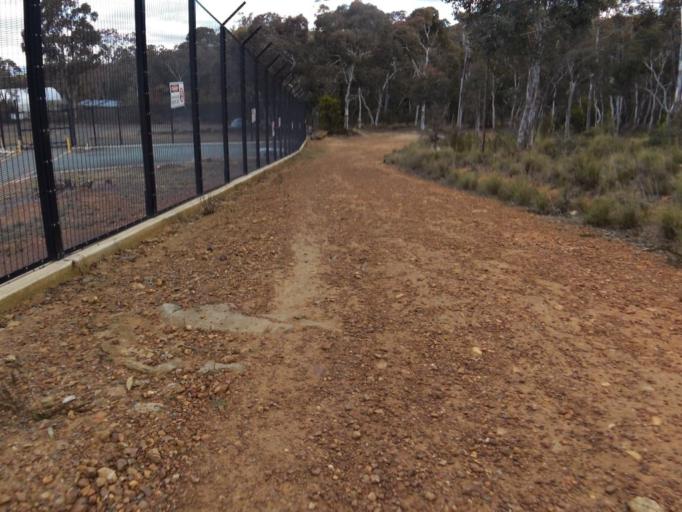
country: AU
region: Australian Capital Territory
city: Acton
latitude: -35.2696
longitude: 149.1083
